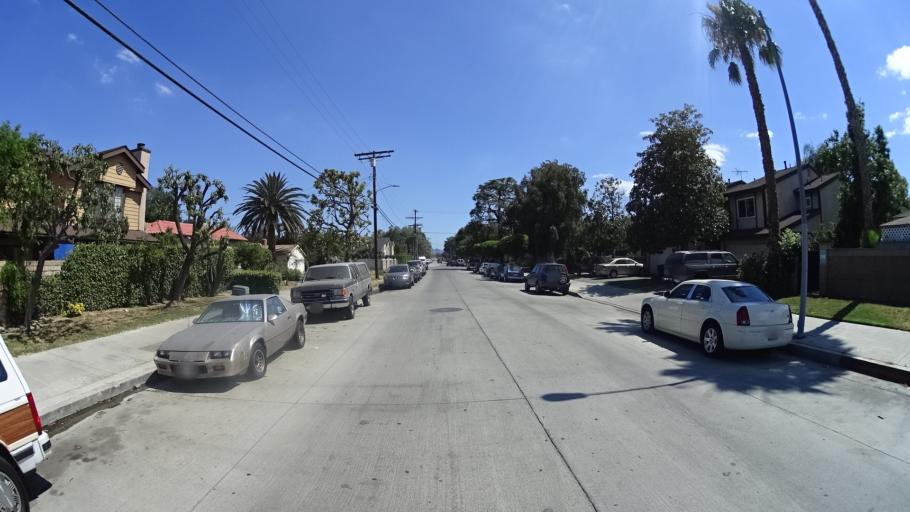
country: US
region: California
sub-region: Los Angeles County
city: Van Nuys
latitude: 34.2255
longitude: -118.4633
